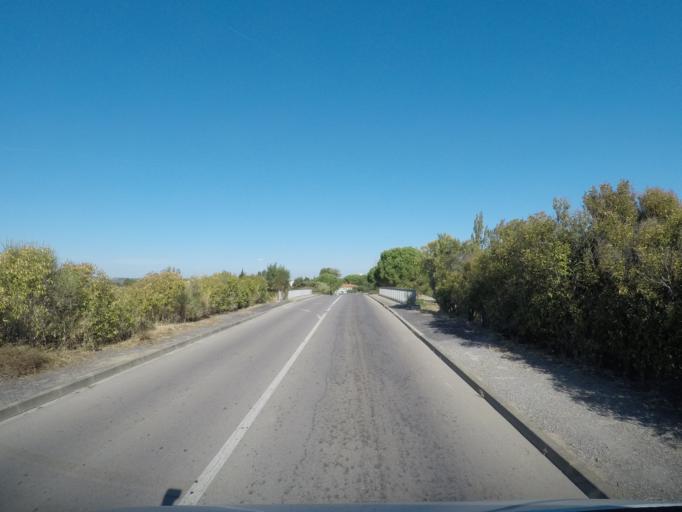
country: FR
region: Languedoc-Roussillon
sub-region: Departement de l'Aude
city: Narbonne
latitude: 43.1720
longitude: 3.0079
